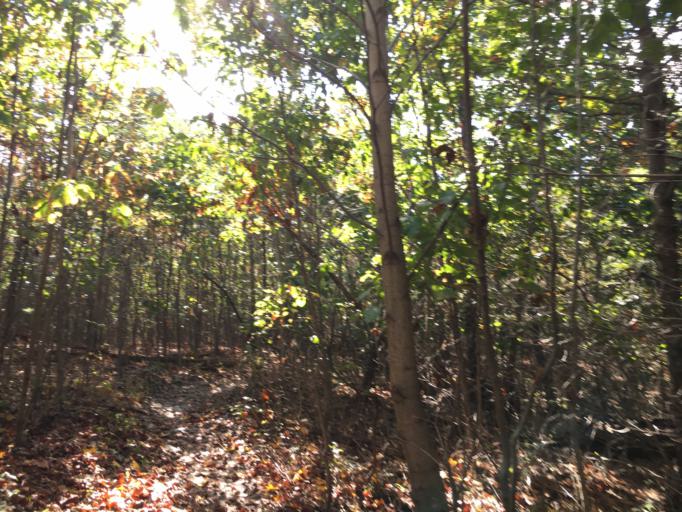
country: US
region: Pennsylvania
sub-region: York County
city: Yorklyn
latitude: 40.0095
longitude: -76.6473
